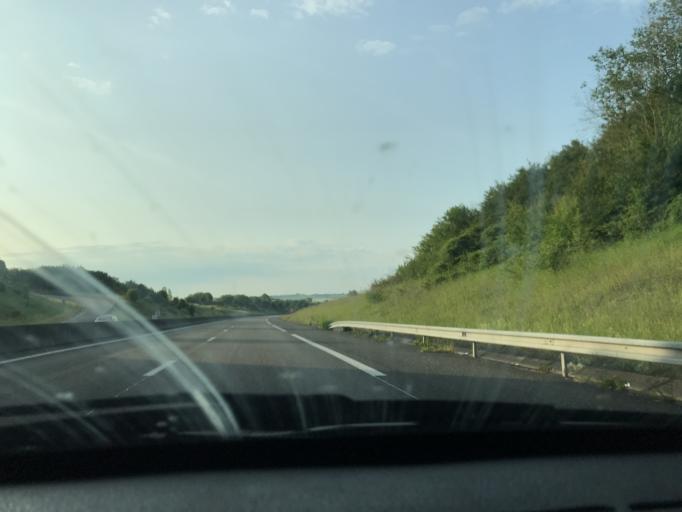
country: FR
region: Lorraine
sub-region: Departement de la Moselle
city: Faulquemont
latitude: 49.0533
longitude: 6.6194
